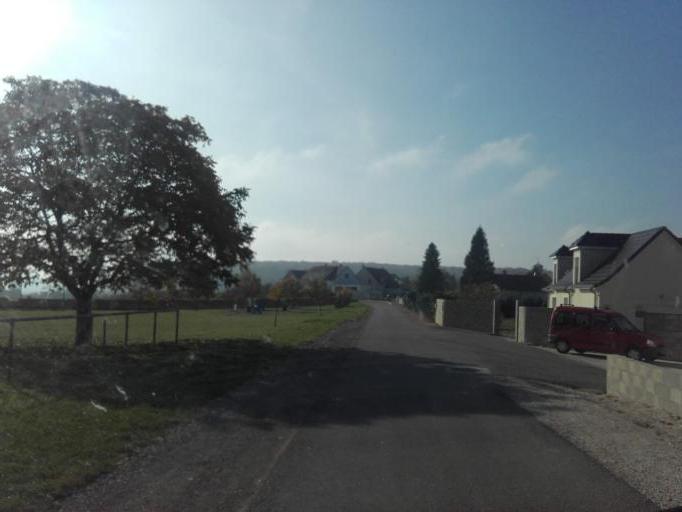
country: FR
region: Bourgogne
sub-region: Departement de la Cote-d'Or
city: Nuits-Saint-Georges
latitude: 47.1301
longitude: 4.9115
